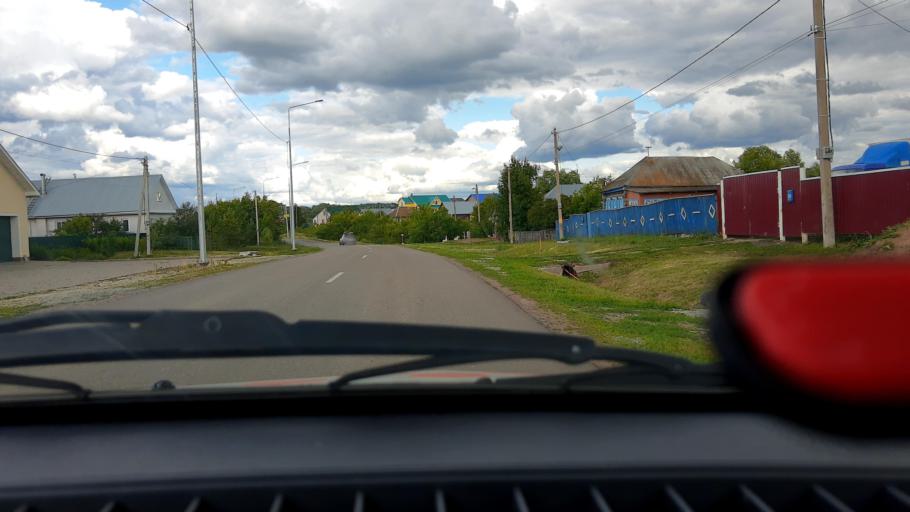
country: RU
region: Bashkortostan
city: Kabakovo
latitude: 54.5026
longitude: 55.9209
